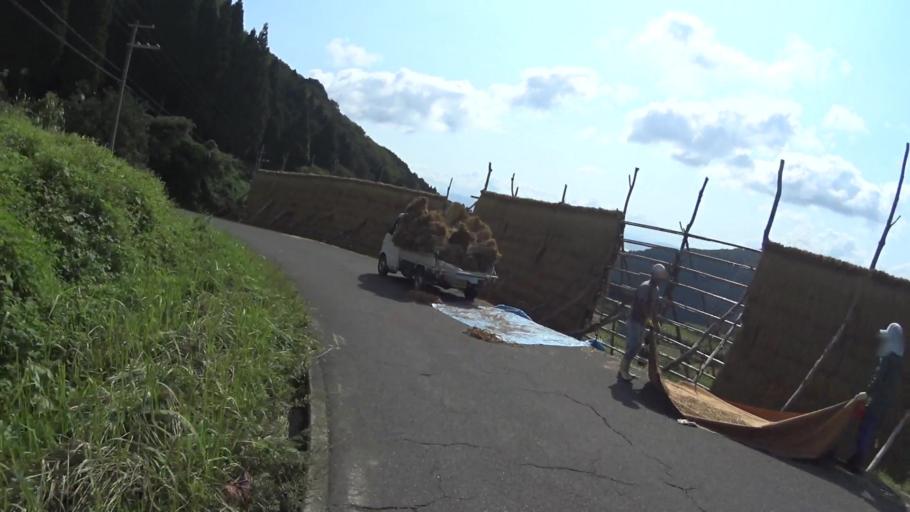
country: JP
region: Kyoto
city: Miyazu
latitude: 35.6411
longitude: 135.1885
